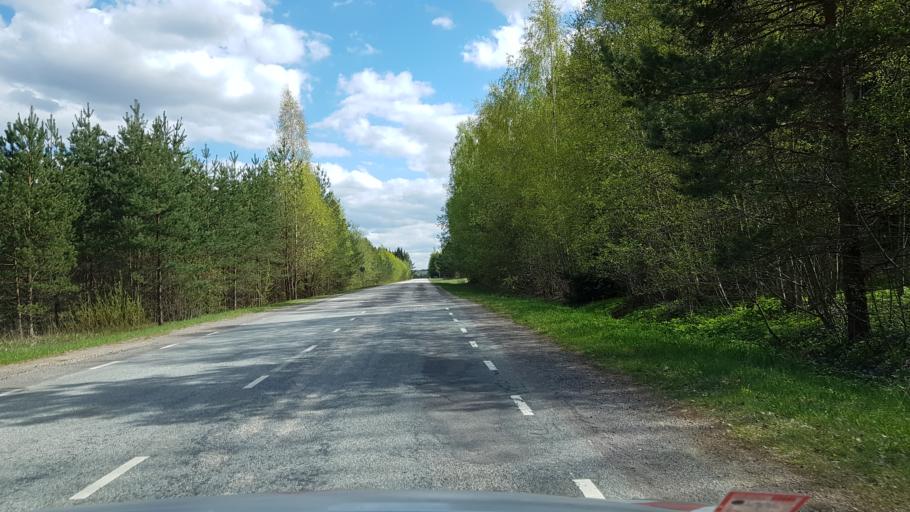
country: EE
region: Tartu
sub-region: UElenurme vald
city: Ulenurme
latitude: 58.2896
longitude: 26.8951
